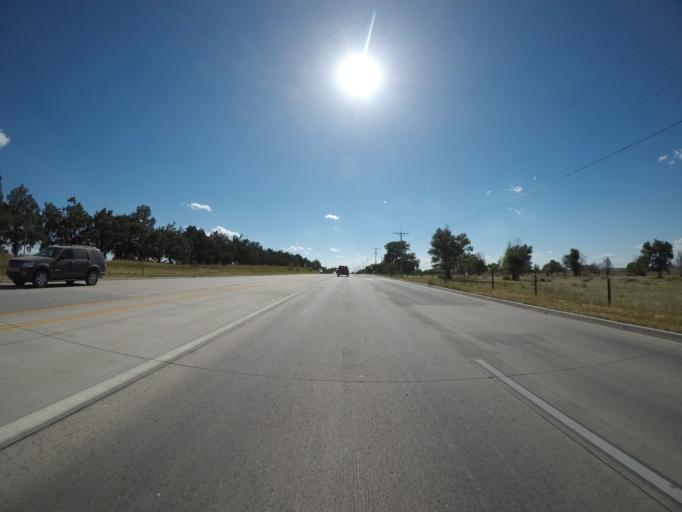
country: US
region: Colorado
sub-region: Logan County
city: Sterling
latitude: 40.6243
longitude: -103.2510
